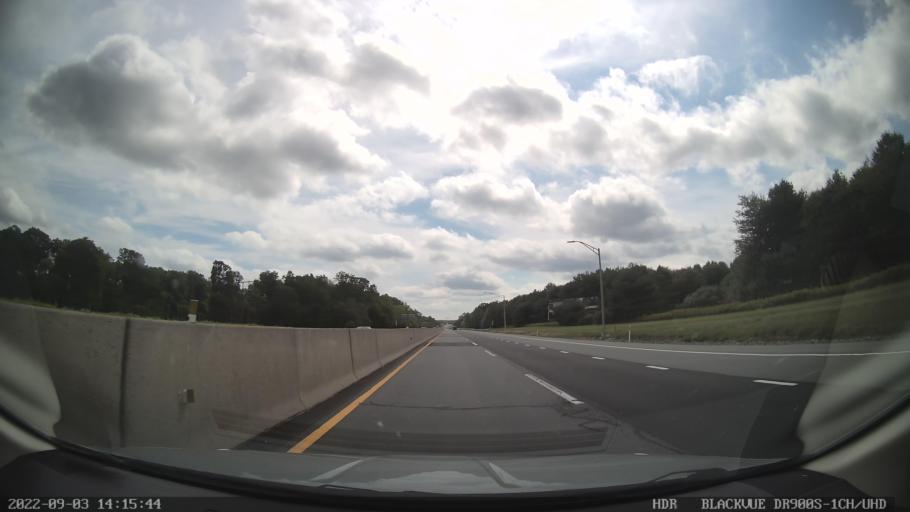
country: US
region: Pennsylvania
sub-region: Carbon County
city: Towamensing Trails
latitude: 40.9665
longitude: -75.6301
